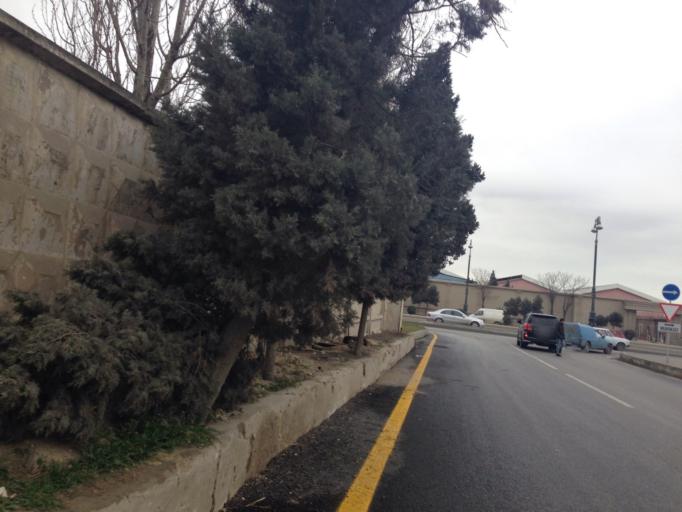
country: AZ
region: Baki
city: Baku
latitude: 40.4086
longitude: 49.8903
